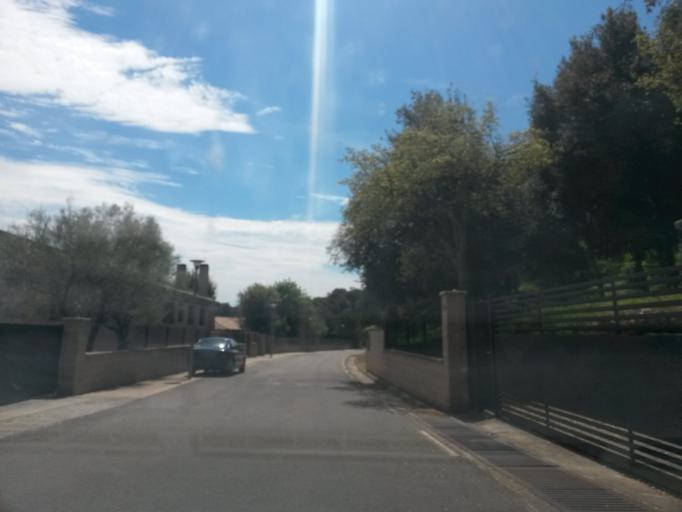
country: ES
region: Catalonia
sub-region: Provincia de Girona
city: Vilablareix
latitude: 41.9656
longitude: 2.7590
